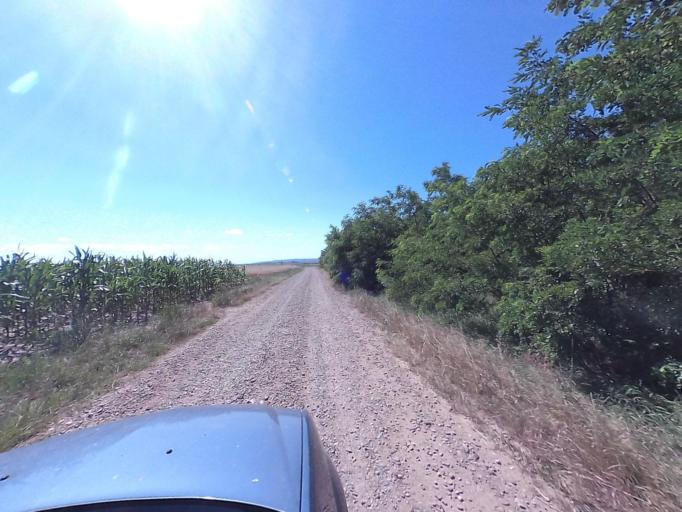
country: RO
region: Vaslui
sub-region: Comuna Costesti
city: Costesti
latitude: 46.4831
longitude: 27.7733
